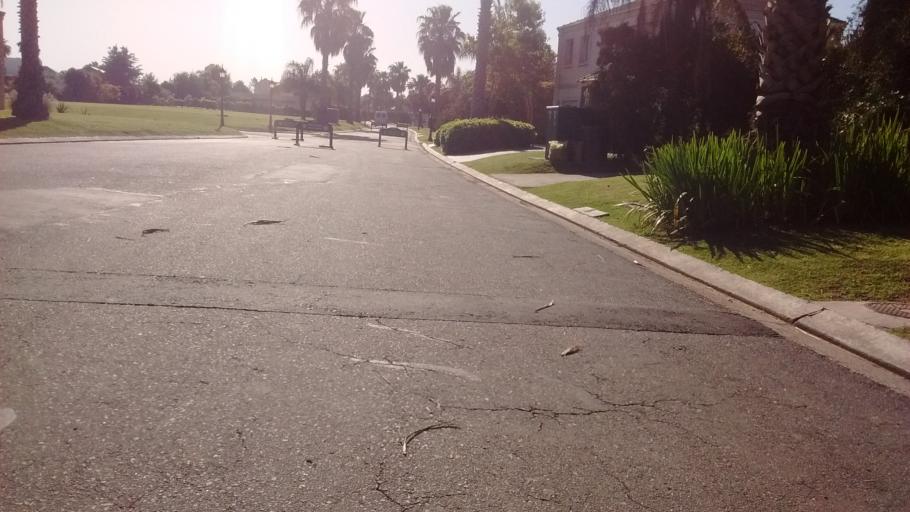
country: AR
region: Santa Fe
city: Funes
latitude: -32.9260
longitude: -60.8240
